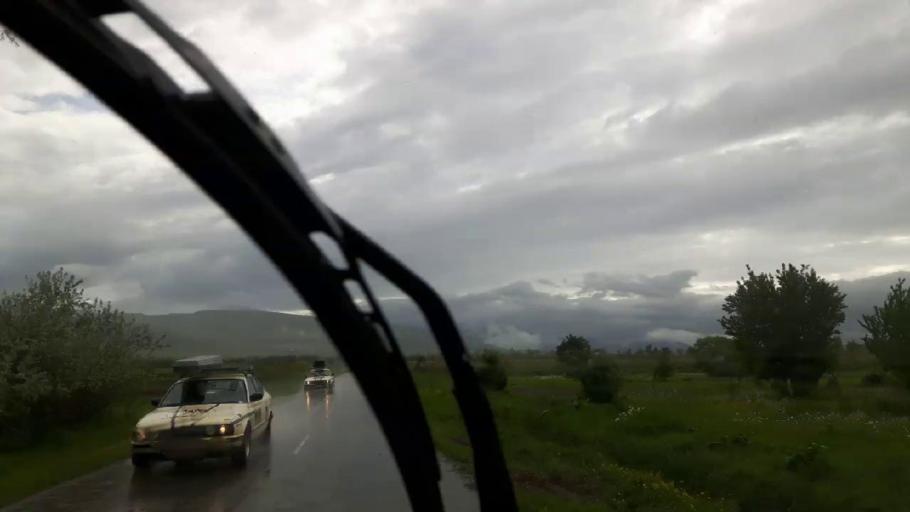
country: GE
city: Agara
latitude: 42.0006
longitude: 43.7533
